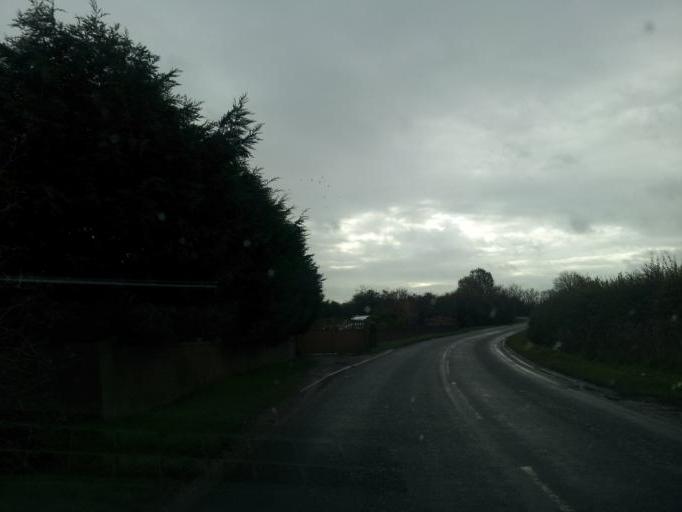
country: GB
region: England
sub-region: Lincolnshire
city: Long Bennington
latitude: 53.0135
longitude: -0.8042
